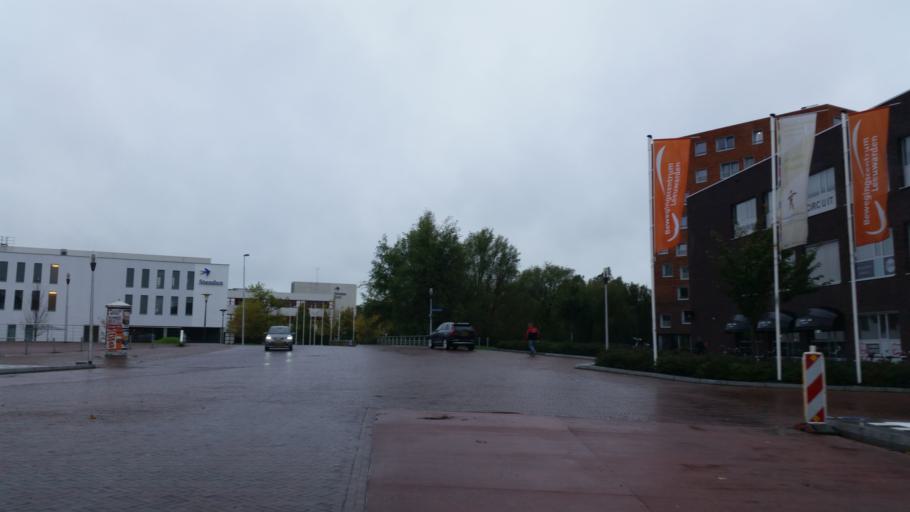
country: NL
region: Friesland
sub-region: Gemeente Leeuwarden
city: Bilgaard
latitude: 53.2119
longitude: 5.7971
